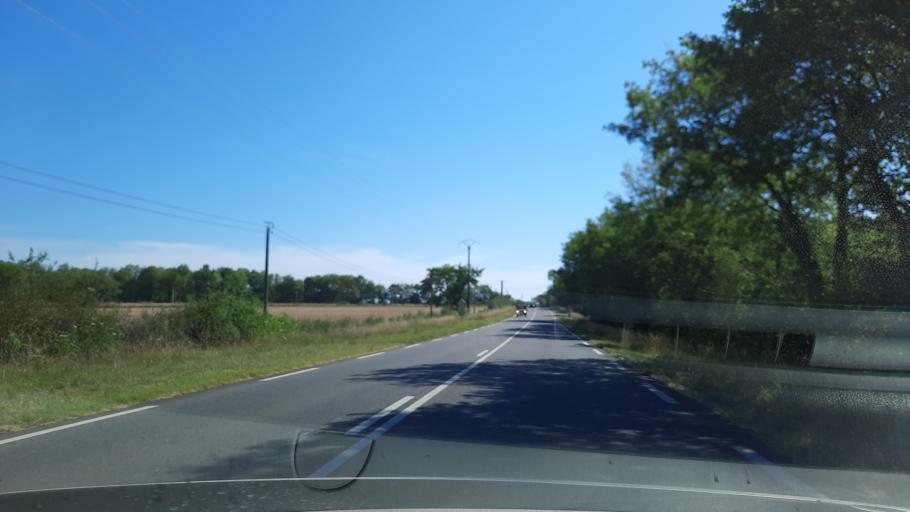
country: FR
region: Midi-Pyrenees
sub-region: Departement du Tarn-et-Garonne
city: Caylus
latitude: 44.2064
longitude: 1.7159
